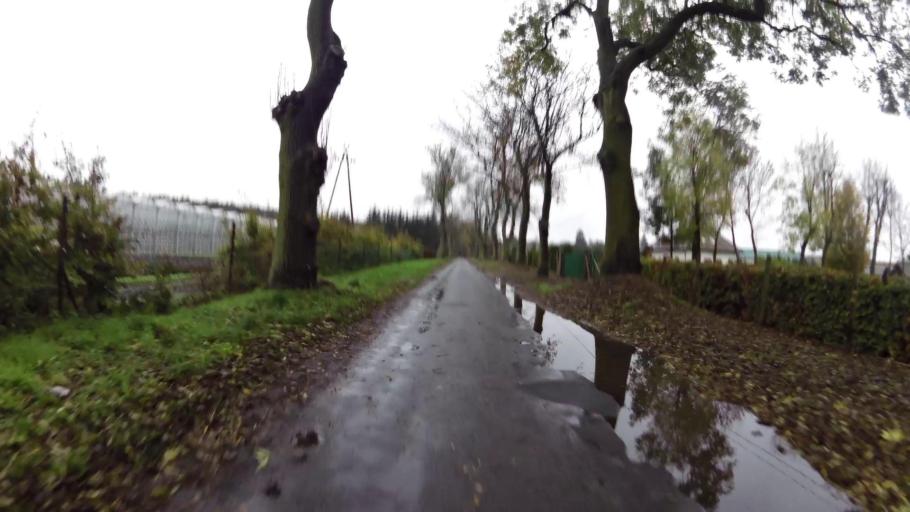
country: PL
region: West Pomeranian Voivodeship
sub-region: Powiat gryfinski
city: Gryfino
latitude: 53.2296
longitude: 14.5228
